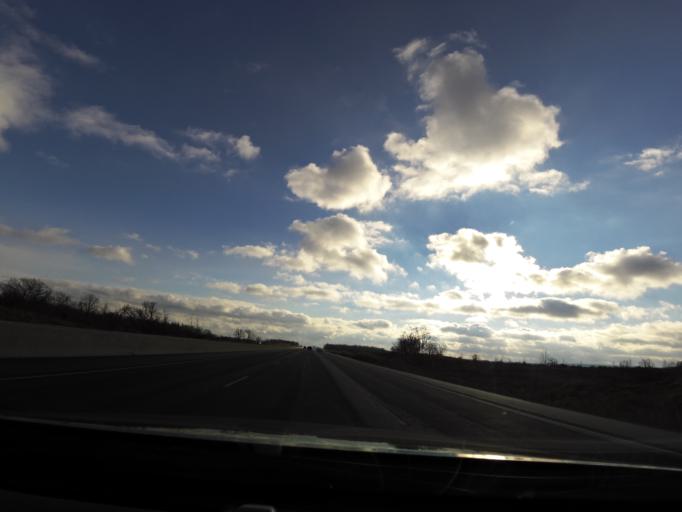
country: CA
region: Ontario
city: Burlington
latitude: 43.4634
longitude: -79.7855
